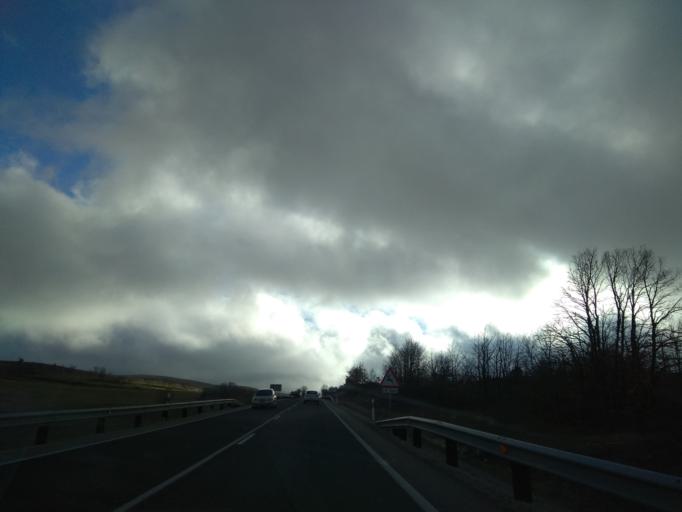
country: ES
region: Castille and Leon
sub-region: Provincia de Burgos
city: Basconcillos del Tozo
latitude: 42.6743
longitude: -3.9366
